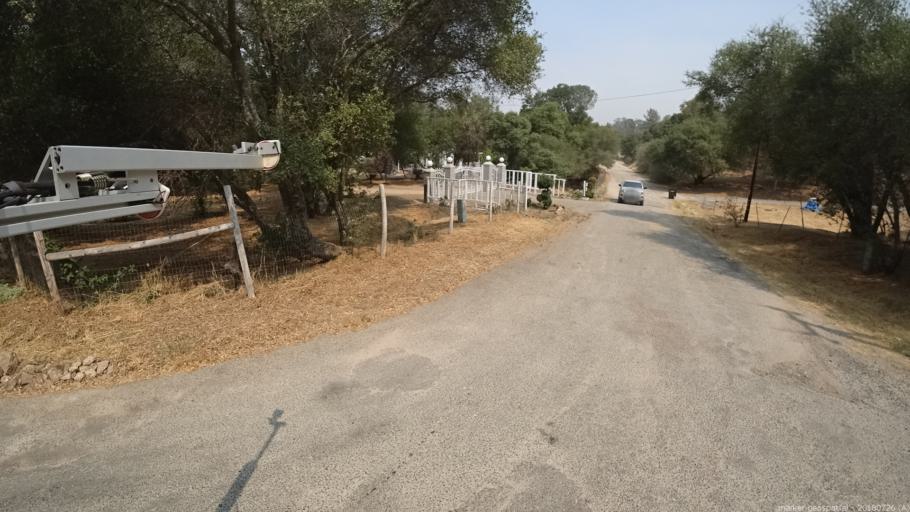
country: US
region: California
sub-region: Madera County
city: Coarsegold
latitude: 37.2387
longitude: -119.6978
